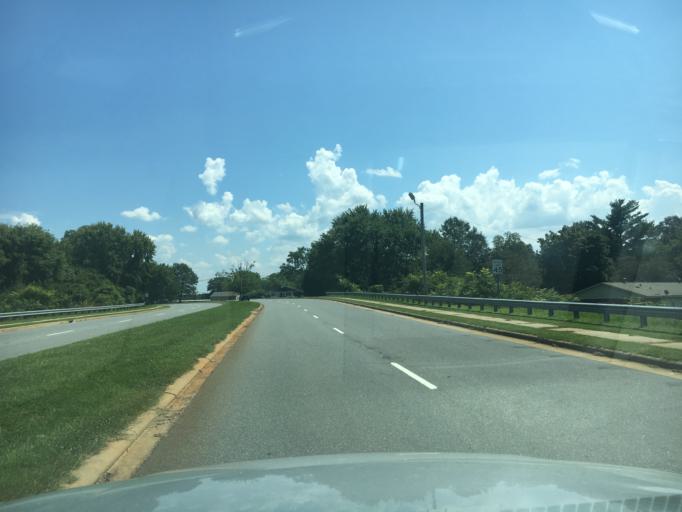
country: US
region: North Carolina
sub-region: Rutherford County
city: Forest City
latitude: 35.3288
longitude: -81.8650
